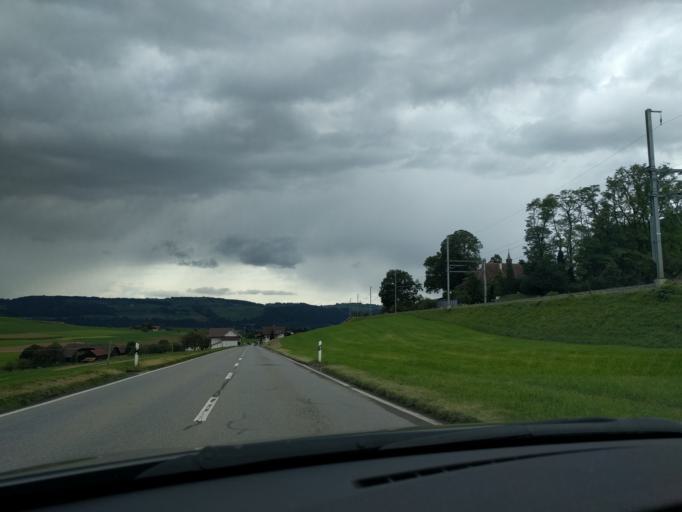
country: CH
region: Bern
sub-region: Bern-Mittelland District
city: Taegertschi
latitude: 46.8772
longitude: 7.6027
